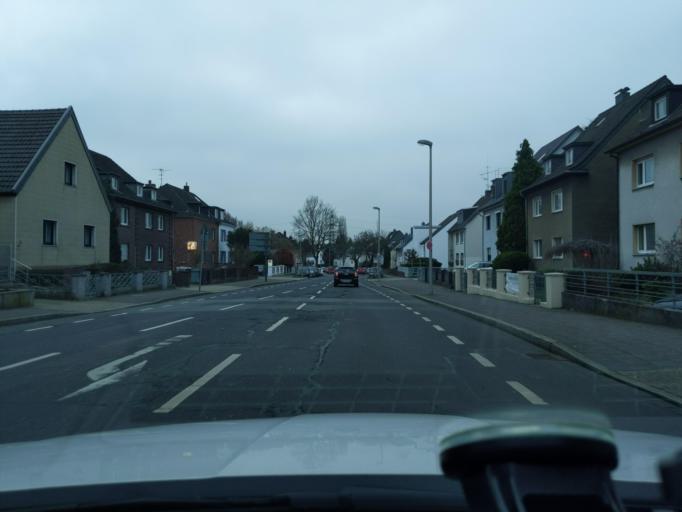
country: DE
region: North Rhine-Westphalia
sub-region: Regierungsbezirk Dusseldorf
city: Dusseldorf
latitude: 51.1838
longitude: 6.8208
